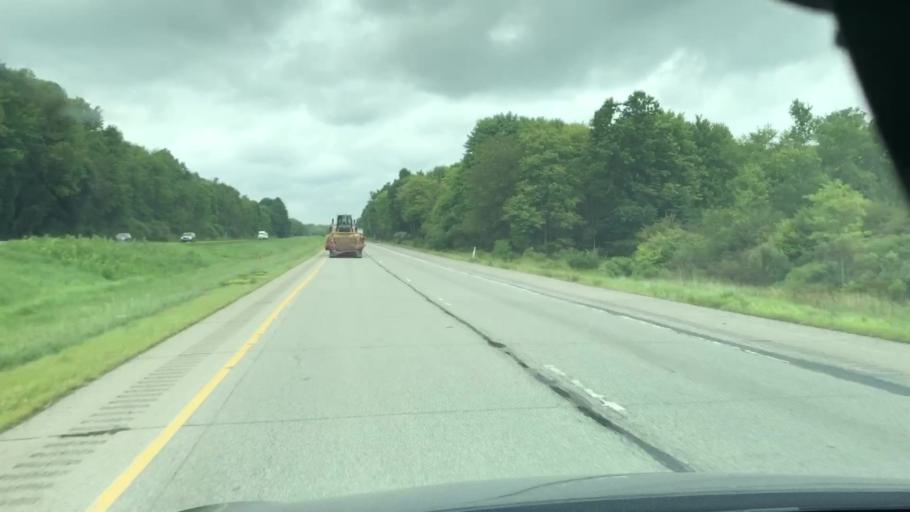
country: US
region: Pennsylvania
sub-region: Butler County
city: Slippery Rock
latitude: 41.0782
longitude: -80.1305
